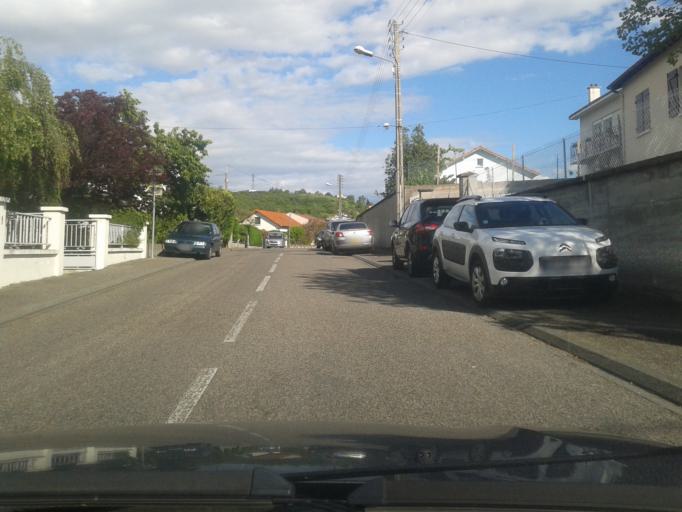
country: FR
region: Auvergne
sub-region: Departement du Puy-de-Dome
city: Aubiere
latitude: 45.7452
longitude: 3.1049
